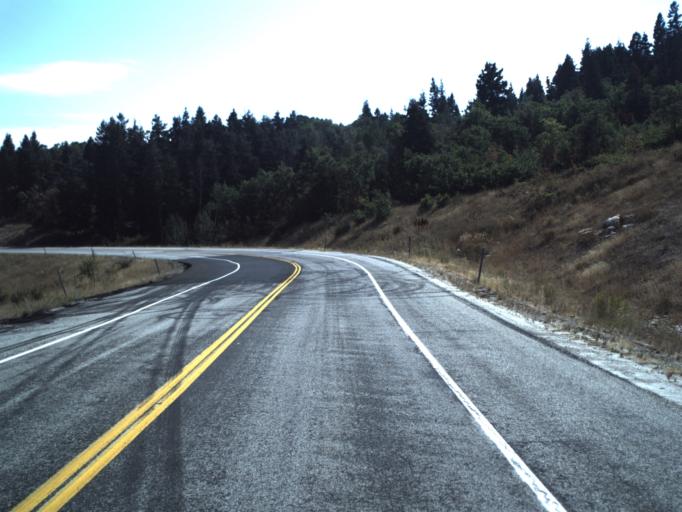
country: US
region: Utah
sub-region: Morgan County
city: Mountain Green
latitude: 41.2053
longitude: -111.8348
